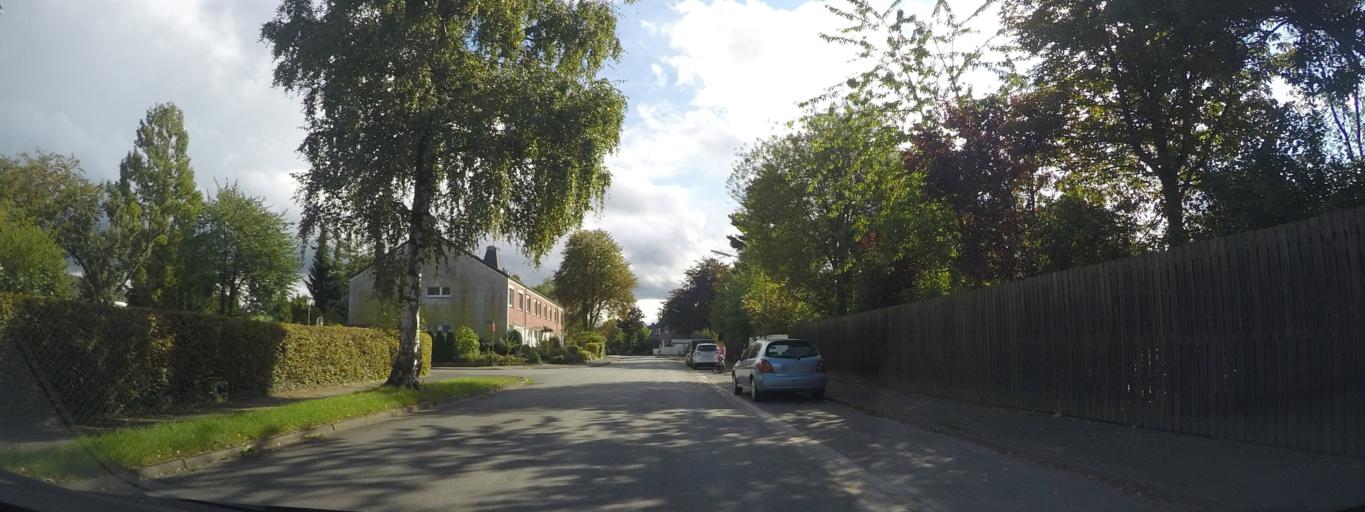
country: DE
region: North Rhine-Westphalia
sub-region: Regierungsbezirk Arnsberg
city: Lippstadt
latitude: 51.6879
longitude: 8.3401
